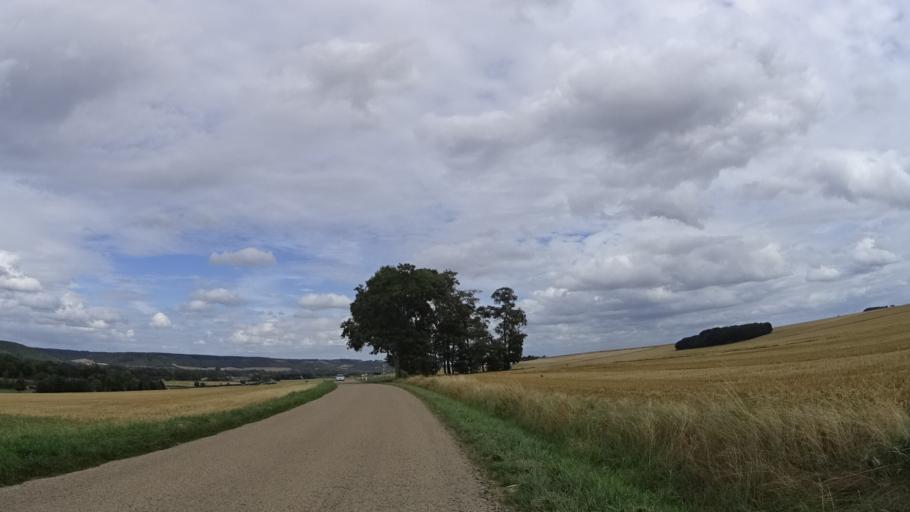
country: FR
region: Bourgogne
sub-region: Departement de l'Yonne
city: Cezy
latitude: 47.9820
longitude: 3.3058
